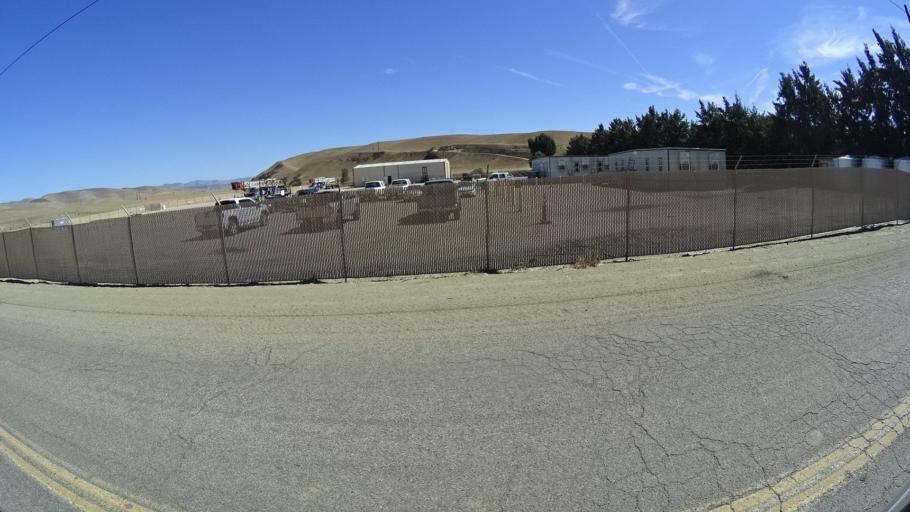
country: US
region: California
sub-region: San Luis Obispo County
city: Lake Nacimiento
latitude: 36.0183
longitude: -120.8854
